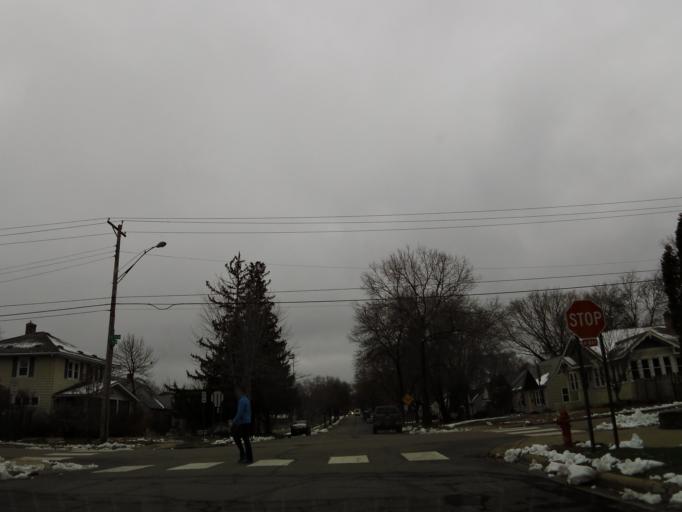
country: US
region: Minnesota
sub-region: Hennepin County
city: Minnetonka Mills
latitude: 44.9260
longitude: -93.4152
